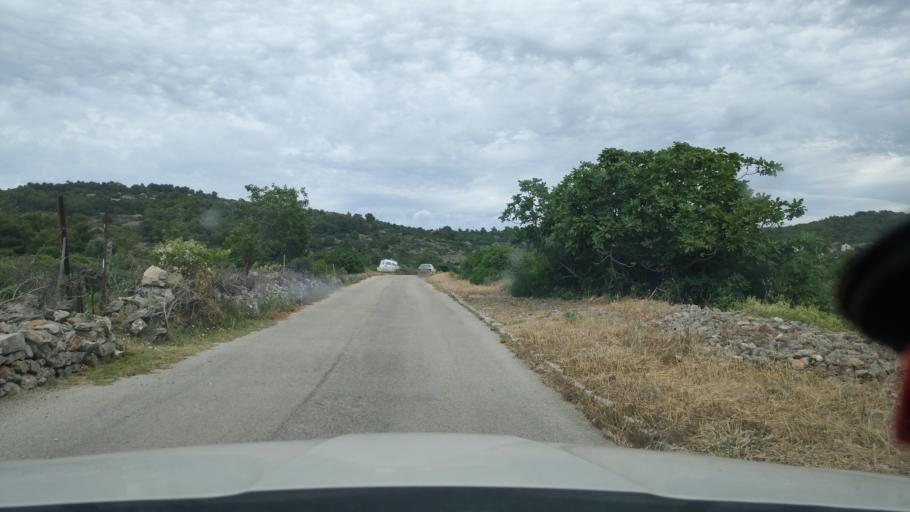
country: HR
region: Splitsko-Dalmatinska
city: Komiza
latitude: 43.0305
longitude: 16.1372
